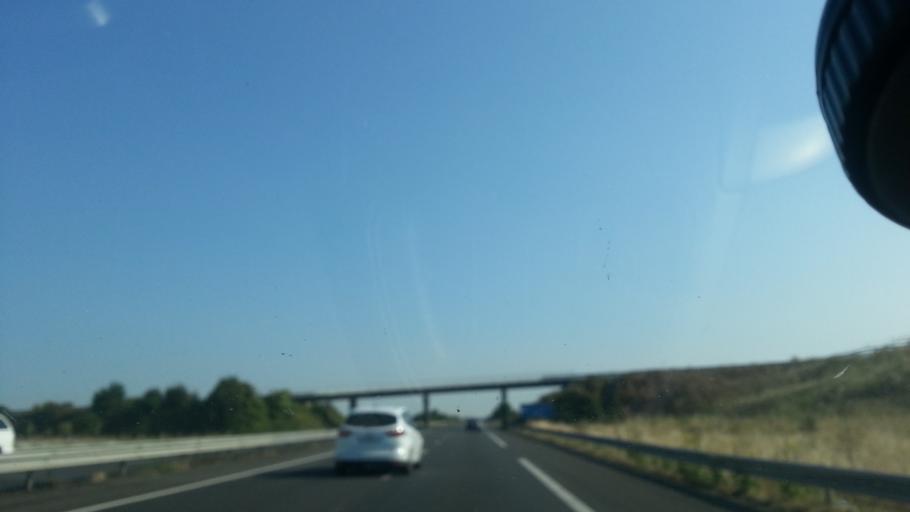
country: FR
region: Centre
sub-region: Departement d'Indre-et-Loire
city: La Celle-Saint-Avant
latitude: 47.0099
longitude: 0.5580
